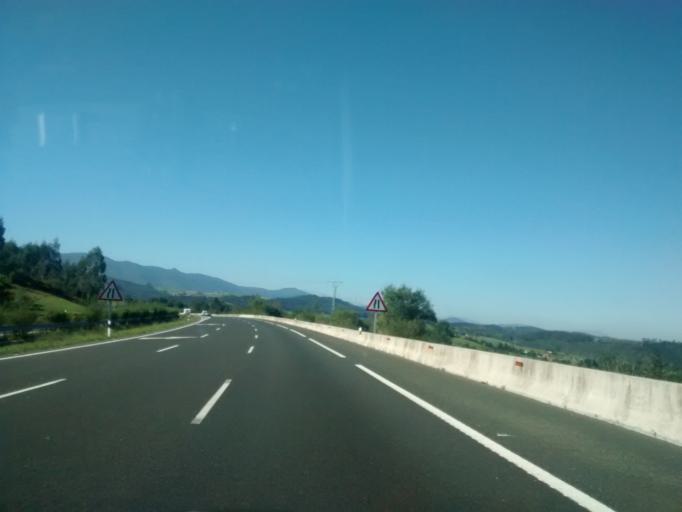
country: ES
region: Cantabria
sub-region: Provincia de Cantabria
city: Cabezon de la Sal
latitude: 43.3224
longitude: -4.2277
